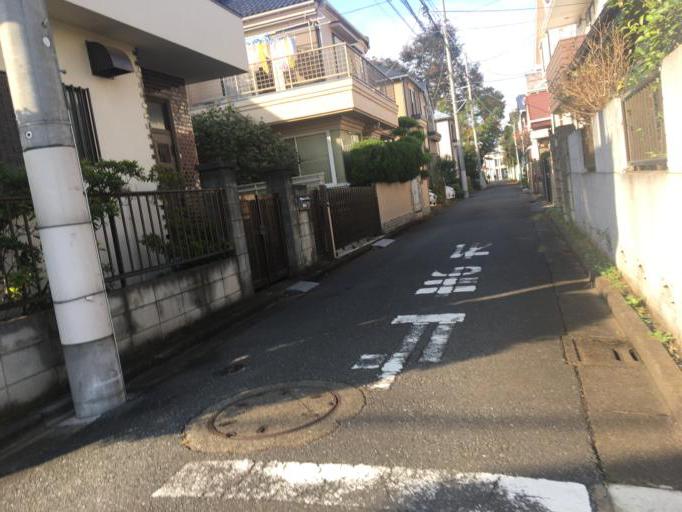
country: JP
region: Tokyo
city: Musashino
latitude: 35.7171
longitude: 139.6016
